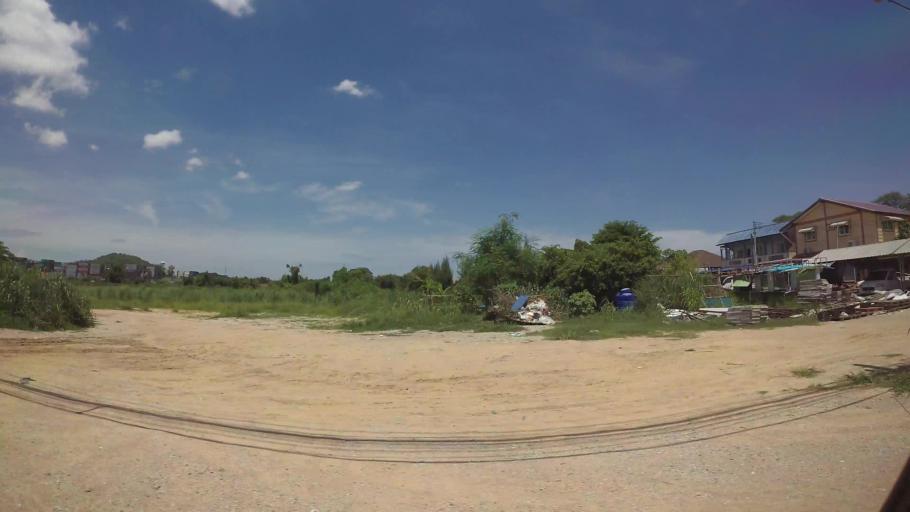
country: TH
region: Chon Buri
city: Si Racha
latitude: 13.1303
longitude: 100.9491
